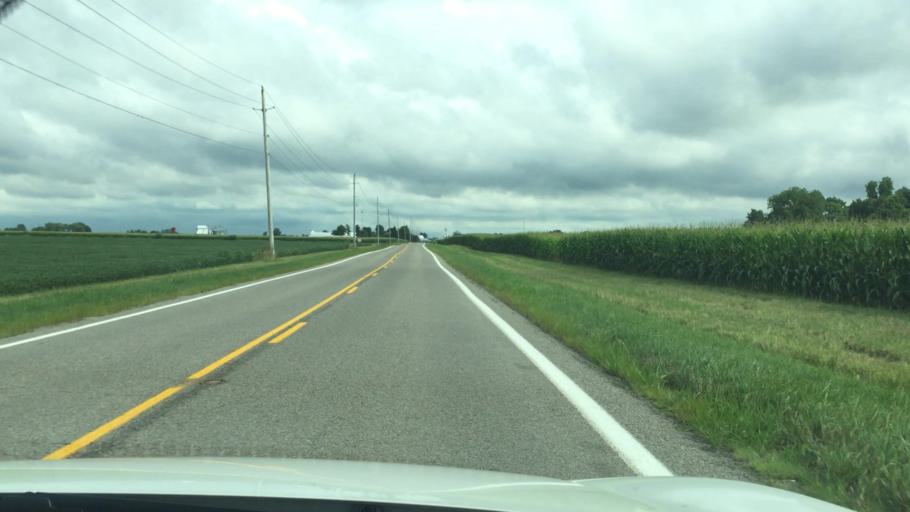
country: US
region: Ohio
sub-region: Champaign County
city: North Lewisburg
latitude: 40.1996
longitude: -83.5308
